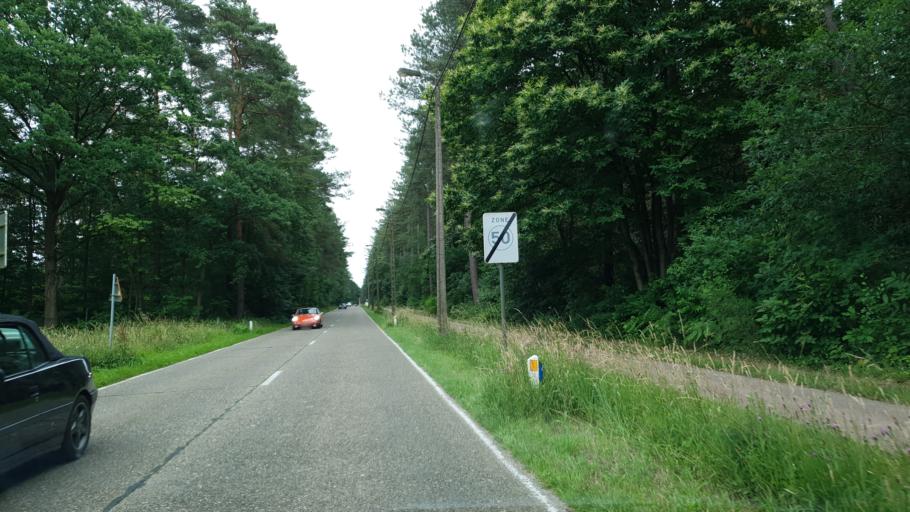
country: BE
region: Flanders
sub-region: Provincie Antwerpen
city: Westerlo
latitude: 51.0593
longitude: 4.9310
